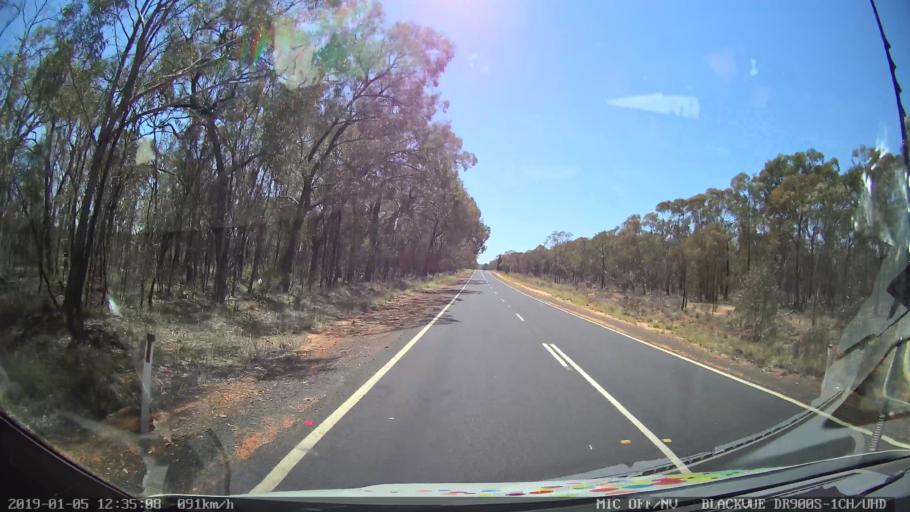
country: AU
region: New South Wales
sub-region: Warrumbungle Shire
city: Coonabarabran
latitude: -31.2104
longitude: 149.4208
